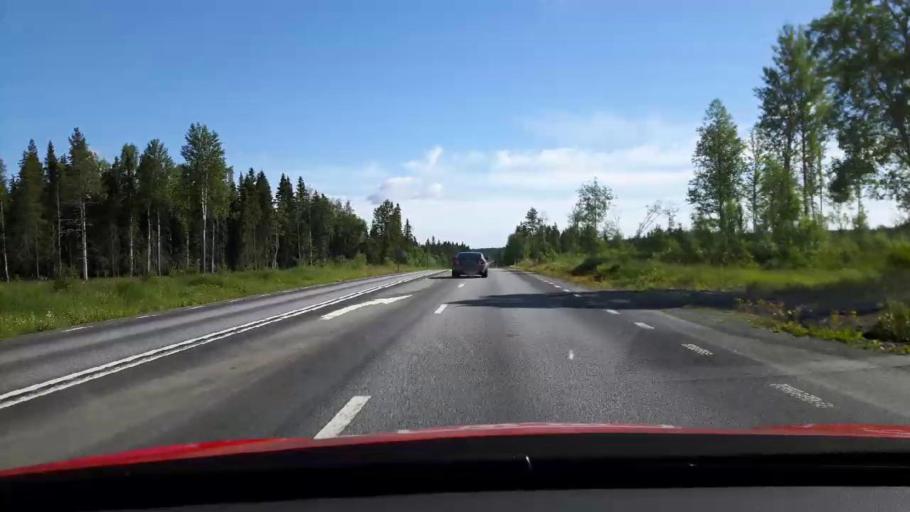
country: SE
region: Jaemtland
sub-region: OEstersunds Kommun
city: Ostersund
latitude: 63.2160
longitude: 14.7281
